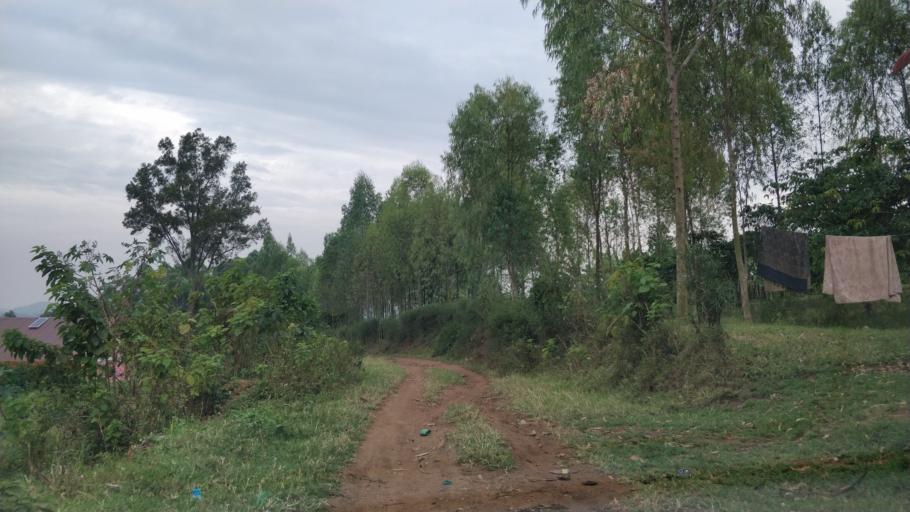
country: UG
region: Western Region
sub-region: Sheema District
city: Kibingo
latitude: -0.7008
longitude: 30.3938
